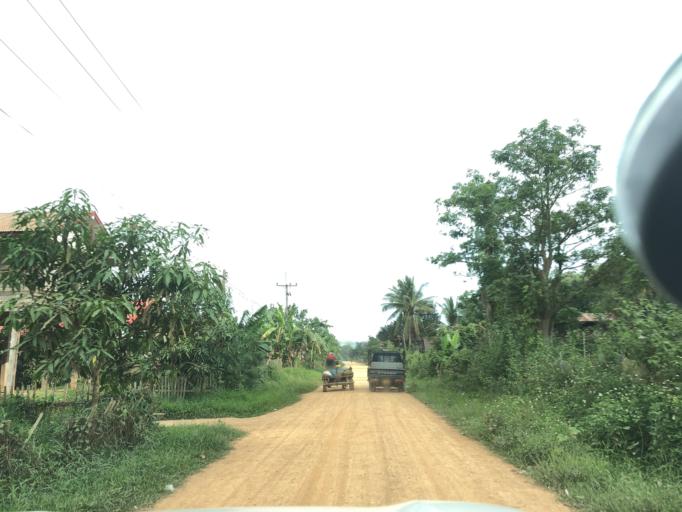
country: TH
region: Loei
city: Chiang Khan
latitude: 18.0165
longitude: 101.4193
